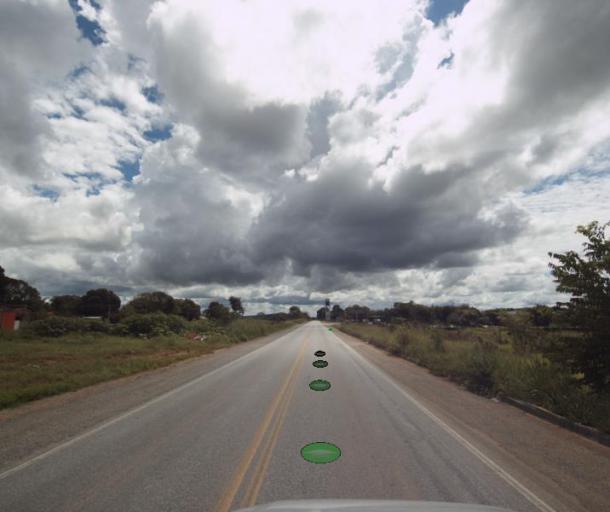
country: BR
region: Goias
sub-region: Uruacu
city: Uruacu
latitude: -14.2846
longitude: -49.1492
